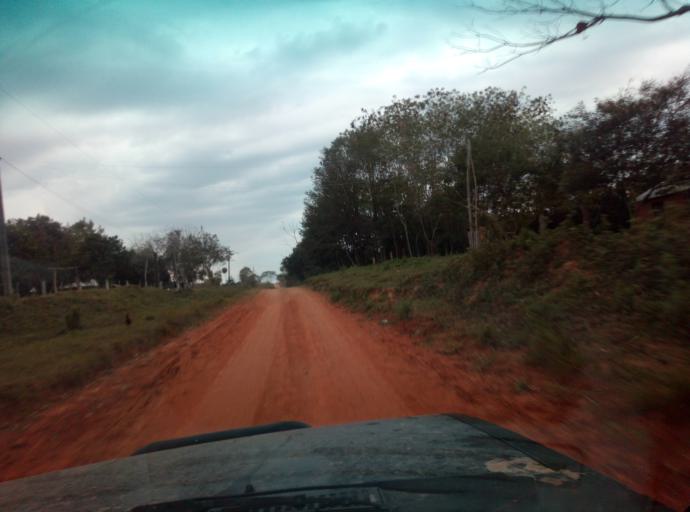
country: PY
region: Caaguazu
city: Doctor Cecilio Baez
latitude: -25.1399
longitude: -56.2238
